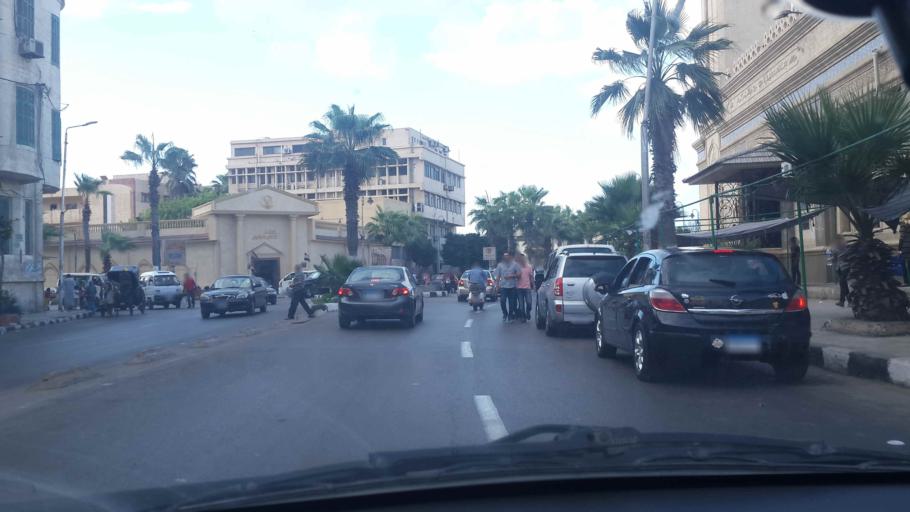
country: EG
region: Alexandria
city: Alexandria
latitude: 31.2095
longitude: 29.8822
